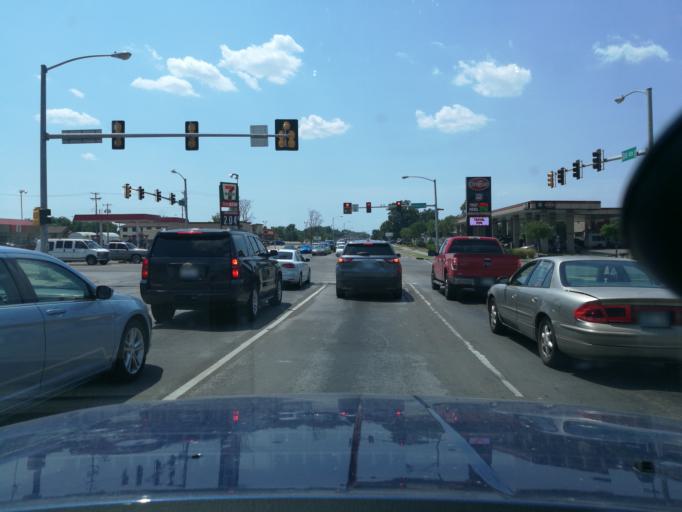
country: US
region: Oklahoma
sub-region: Oklahoma County
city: Oklahoma City
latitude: 35.4208
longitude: -97.5075
